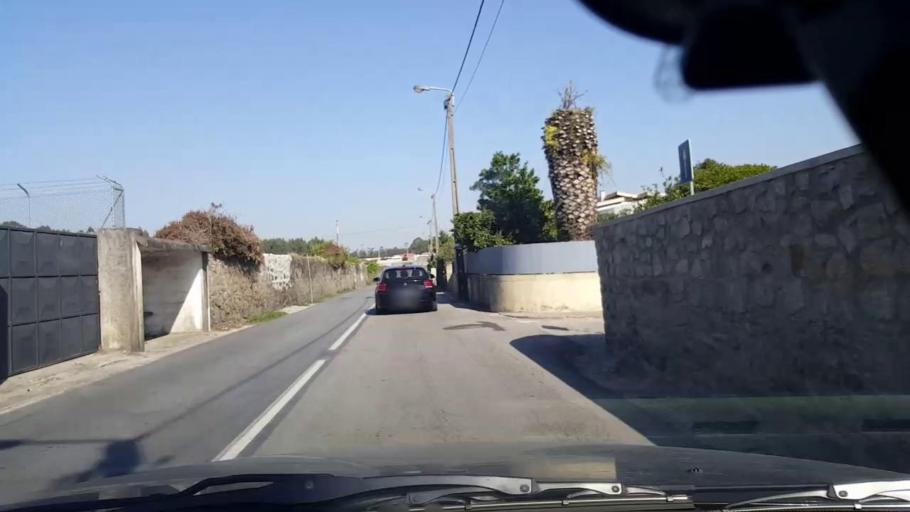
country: PT
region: Porto
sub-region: Vila do Conde
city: Arvore
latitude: 41.3327
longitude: -8.6812
